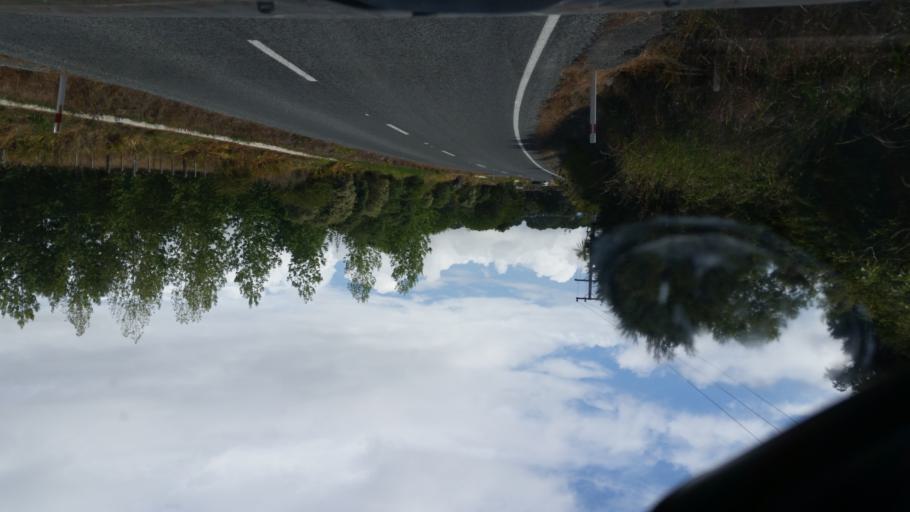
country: NZ
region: Auckland
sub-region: Auckland
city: Wellsford
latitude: -36.1277
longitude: 174.5616
